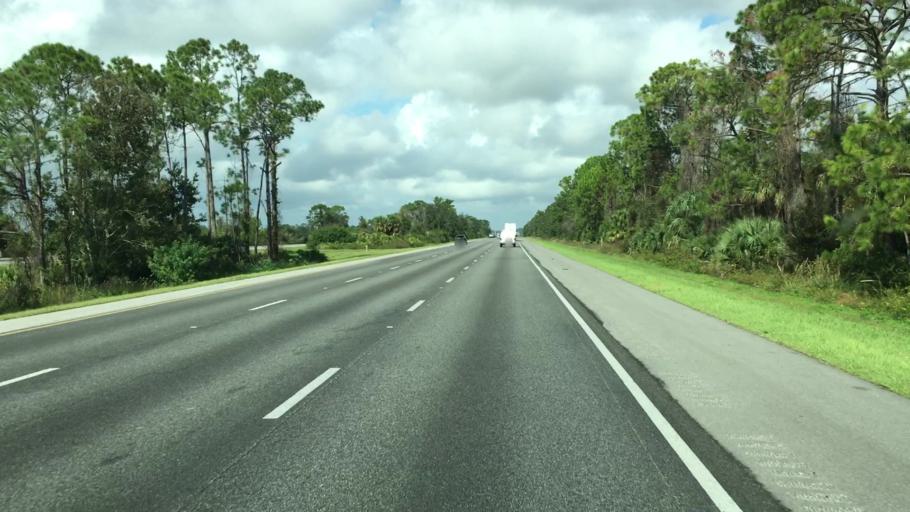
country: US
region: Florida
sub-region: Volusia County
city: Samsula-Spruce Creek
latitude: 29.0734
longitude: -81.0123
